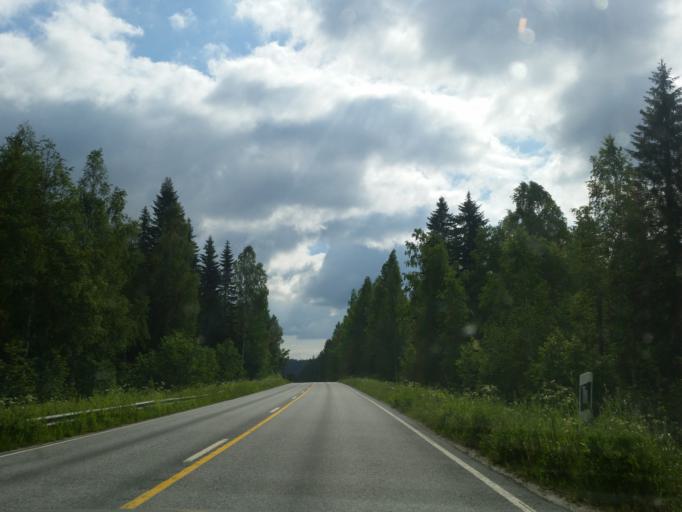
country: FI
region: Northern Savo
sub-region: Kuopio
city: Kuopio
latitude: 62.8446
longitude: 27.4136
